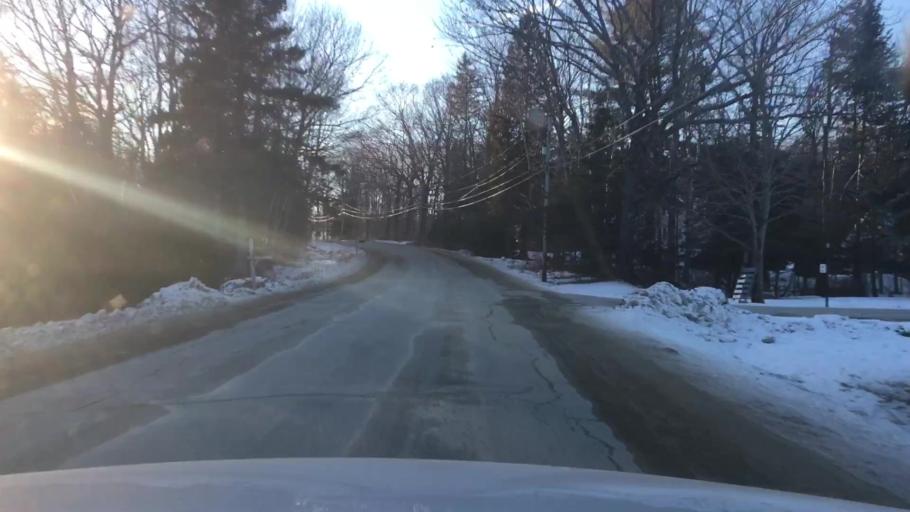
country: US
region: Maine
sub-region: Penobscot County
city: Eddington
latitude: 44.8282
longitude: -68.6536
